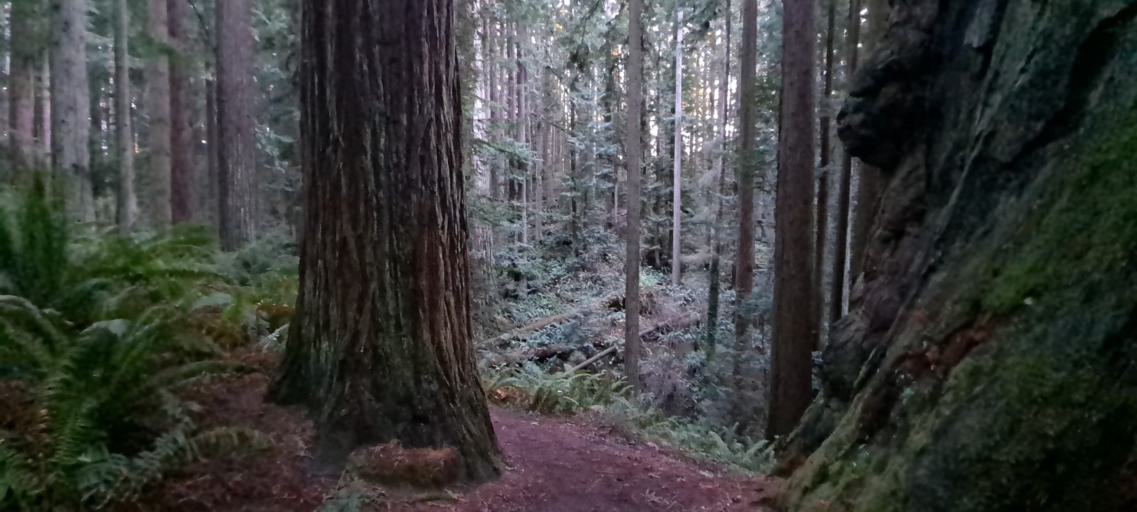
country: US
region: California
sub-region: Humboldt County
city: Arcata
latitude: 40.8715
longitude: -124.0704
